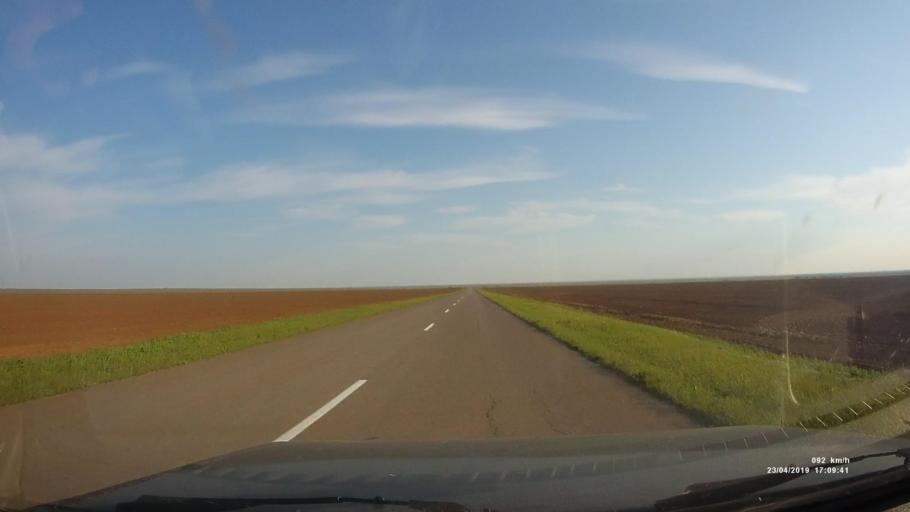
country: RU
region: Kalmykiya
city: Priyutnoye
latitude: 46.2549
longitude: 43.4842
